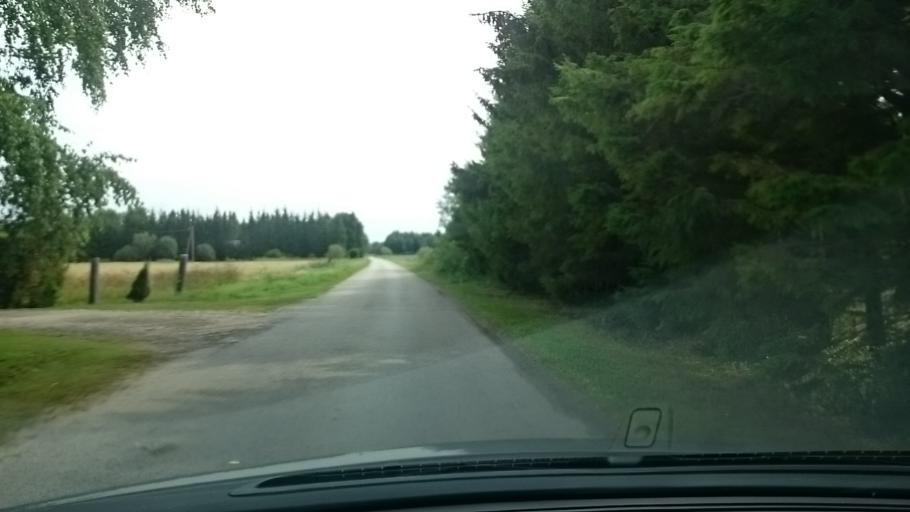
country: EE
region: Laeaene
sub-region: Haapsalu linn
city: Haapsalu
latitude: 59.0098
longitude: 23.5272
